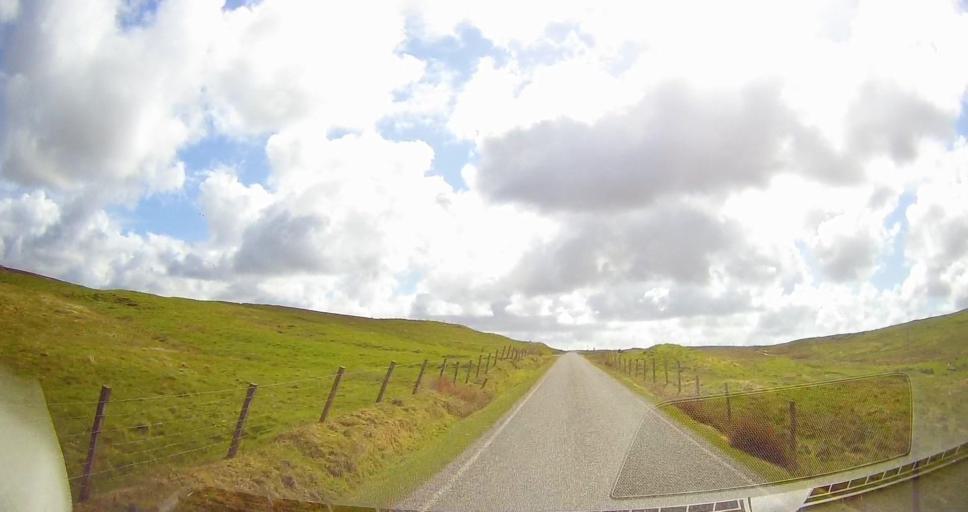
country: GB
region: Scotland
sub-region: Shetland Islands
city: Lerwick
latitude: 60.5240
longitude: -1.3732
